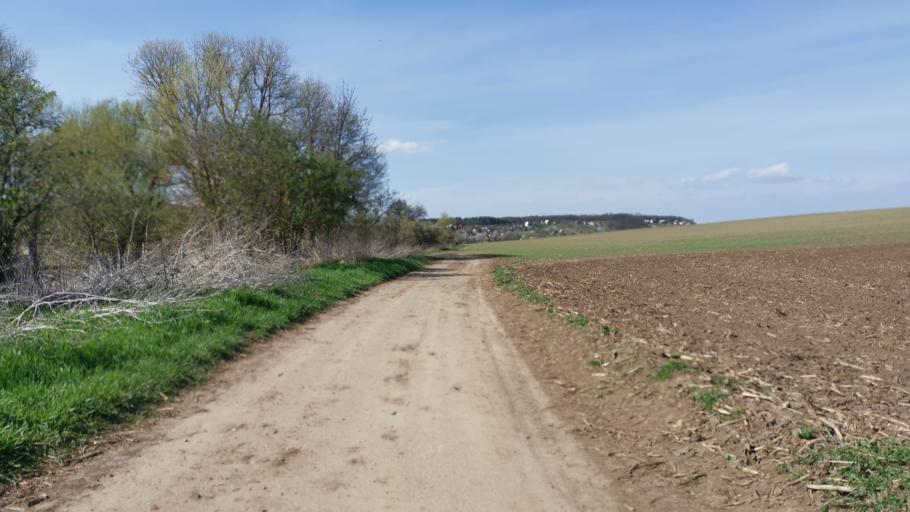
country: SK
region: Trnavsky
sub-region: Okres Skalica
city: Holic
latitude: 48.7839
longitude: 17.1761
